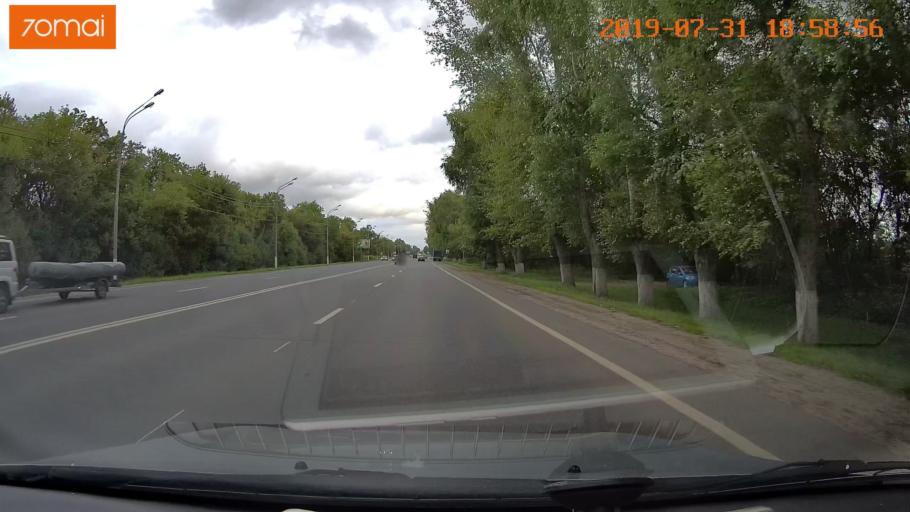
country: RU
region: Moskovskaya
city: Raduzhnyy
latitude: 55.1429
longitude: 38.7102
